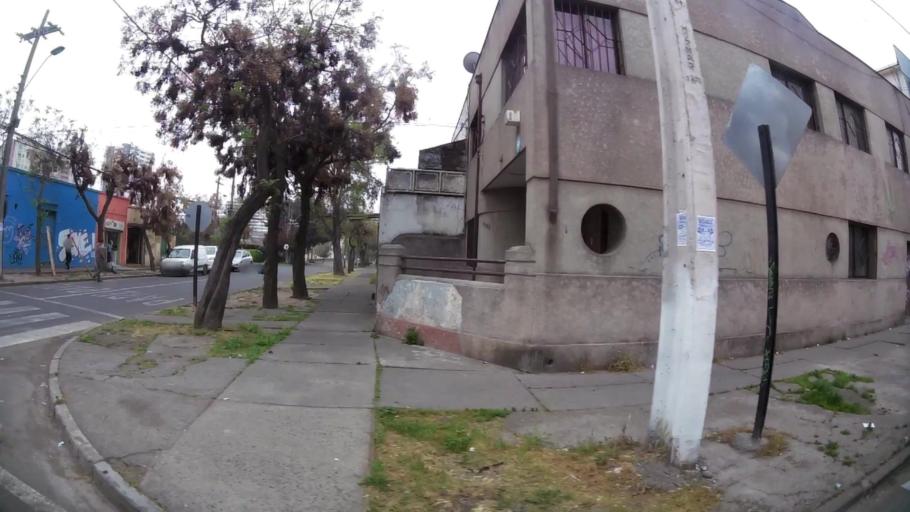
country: CL
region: Santiago Metropolitan
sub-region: Provincia de Santiago
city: Santiago
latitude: -33.4959
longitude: -70.6494
